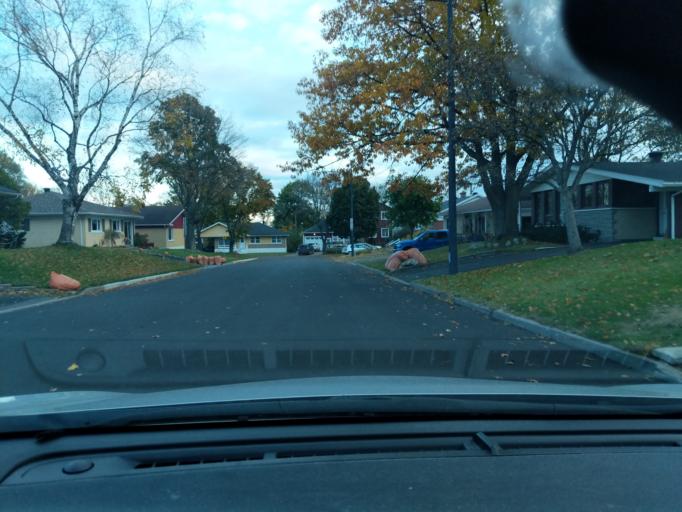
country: CA
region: Quebec
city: L'Ancienne-Lorette
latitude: 46.7641
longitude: -71.2827
